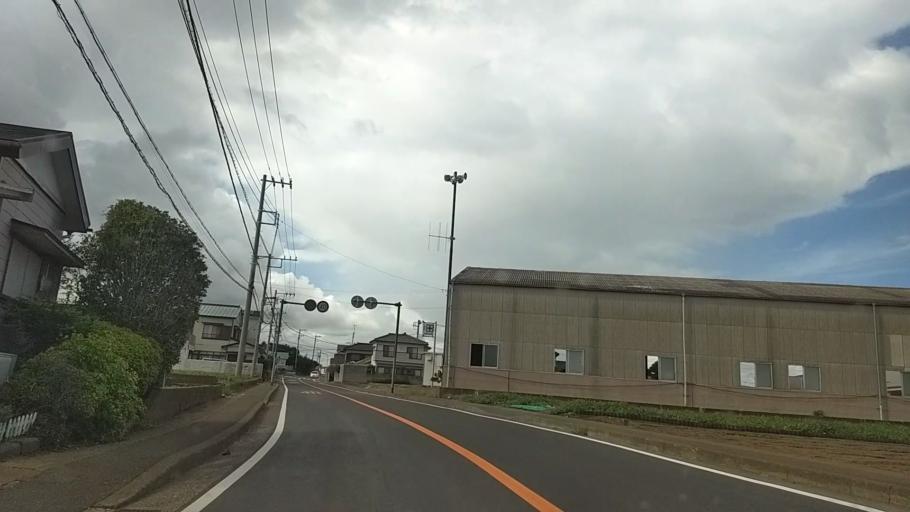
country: JP
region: Kanagawa
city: Miura
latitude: 35.1503
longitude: 139.6688
